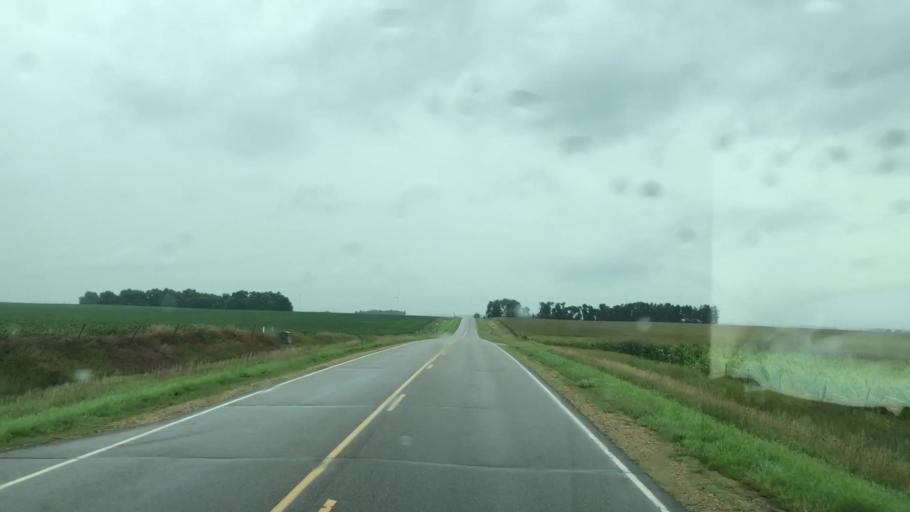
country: US
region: Iowa
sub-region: O'Brien County
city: Sanborn
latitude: 43.2228
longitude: -95.7236
